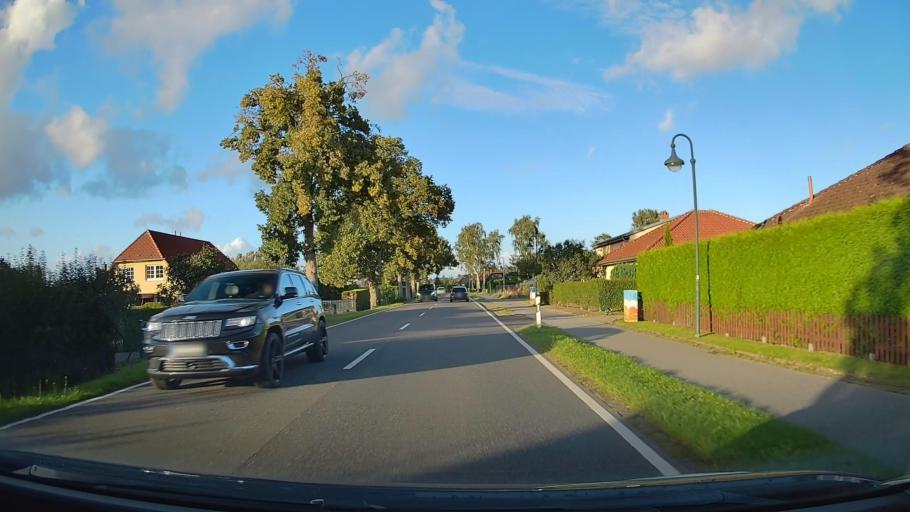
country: DE
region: Mecklenburg-Vorpommern
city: Wendorf
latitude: 54.2546
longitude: 13.0290
